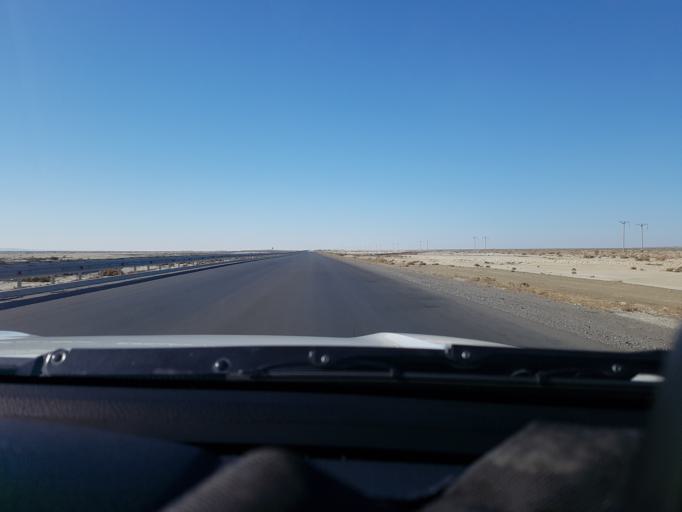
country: TM
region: Balkan
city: Gazanjyk
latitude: 39.2571
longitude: 55.1083
